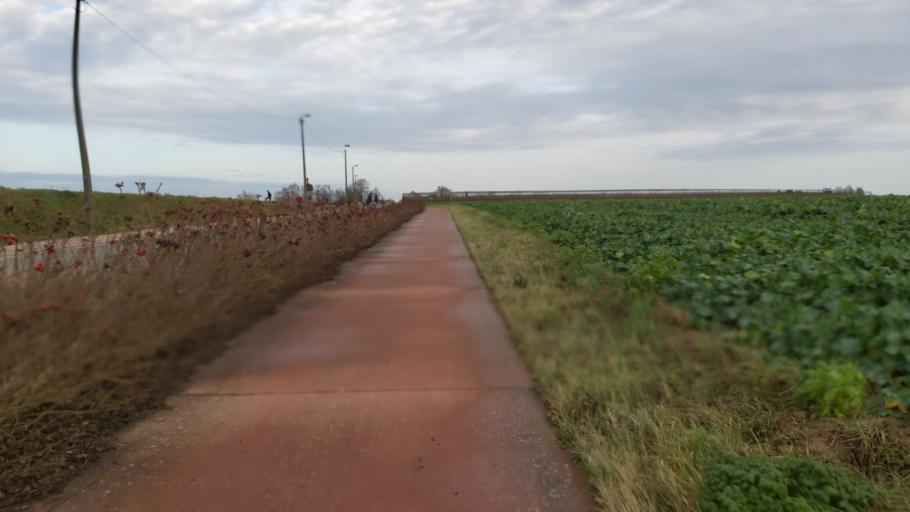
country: BE
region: Flanders
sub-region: Provincie Vlaams-Brabant
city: Tienen
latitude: 50.8290
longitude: 4.9025
